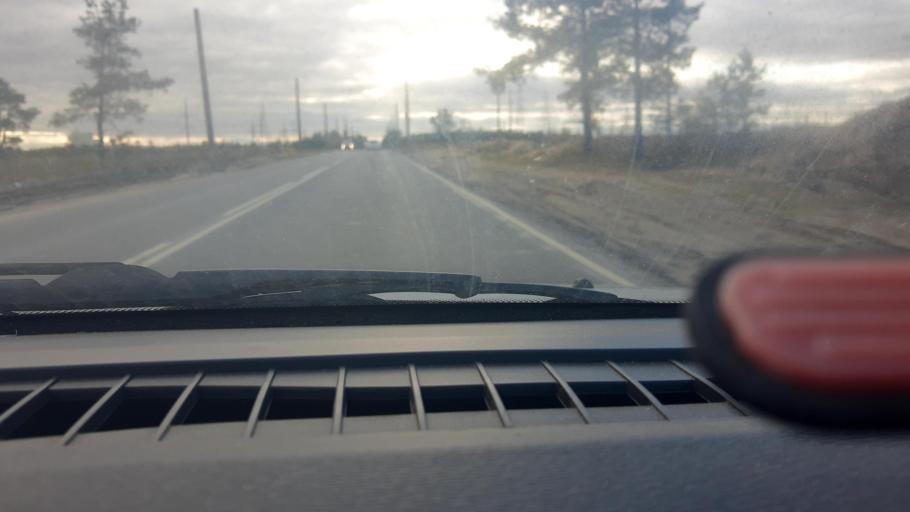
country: RU
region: Nizjnij Novgorod
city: Babino
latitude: 56.2793
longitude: 43.5666
